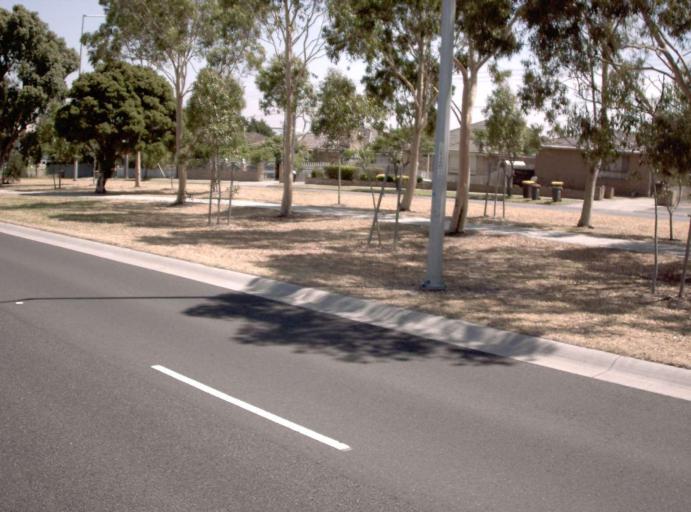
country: AU
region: Victoria
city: Clayton
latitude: -37.9130
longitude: 145.1140
